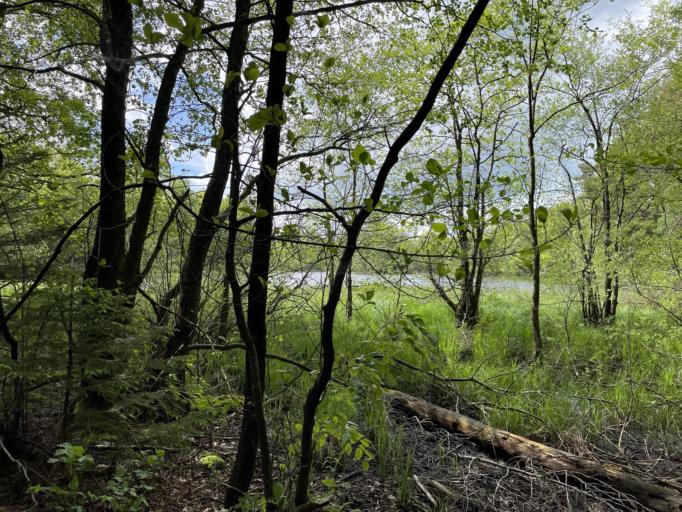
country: SE
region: Skane
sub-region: Klippans Kommun
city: Klippan
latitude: 56.1595
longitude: 13.1639
